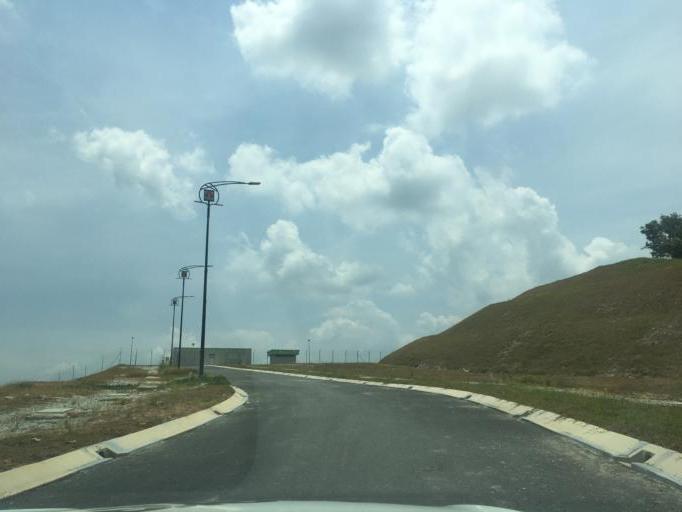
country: MY
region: Putrajaya
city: Putrajaya
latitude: 2.8482
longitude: 101.7103
